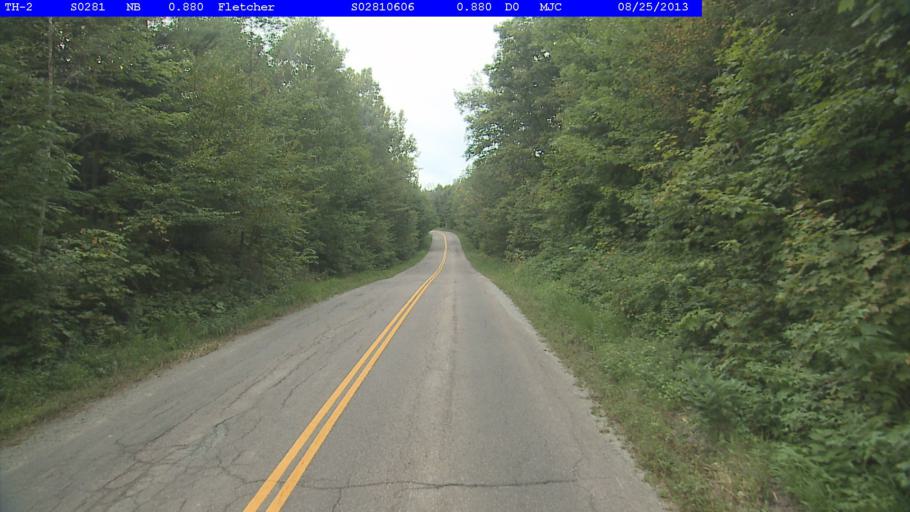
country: US
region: Vermont
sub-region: Chittenden County
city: Milton
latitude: 44.6914
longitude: -72.9267
